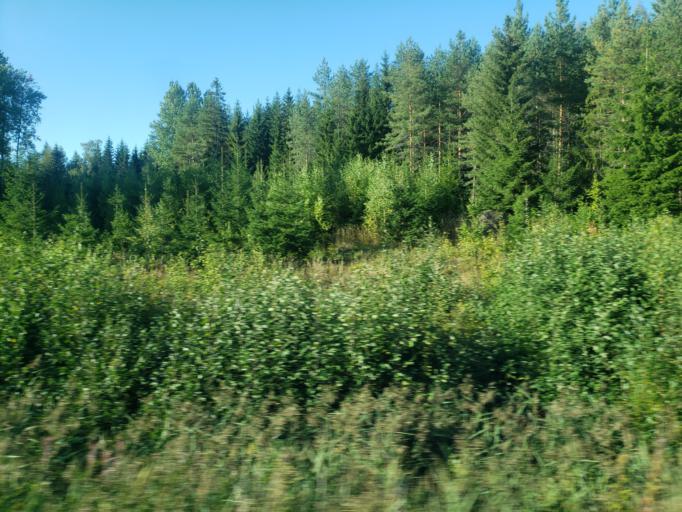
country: FI
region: South Karelia
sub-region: Lappeenranta
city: Lemi
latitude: 60.9378
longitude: 27.8714
